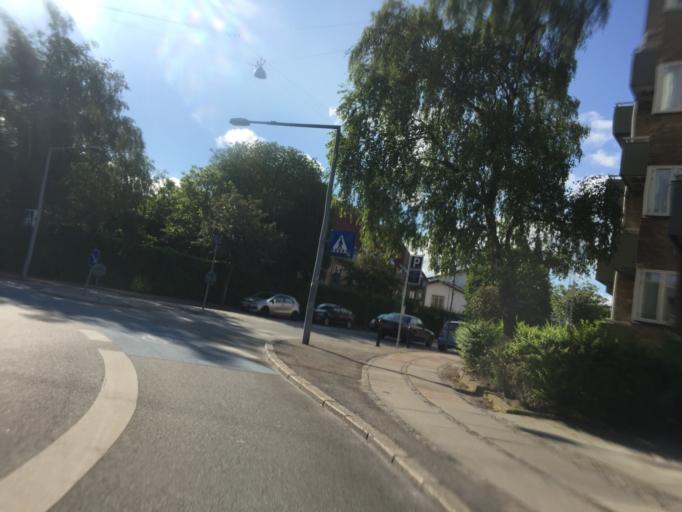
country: DK
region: Capital Region
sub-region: Kobenhavn
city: Vanlose
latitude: 55.6868
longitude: 12.5063
